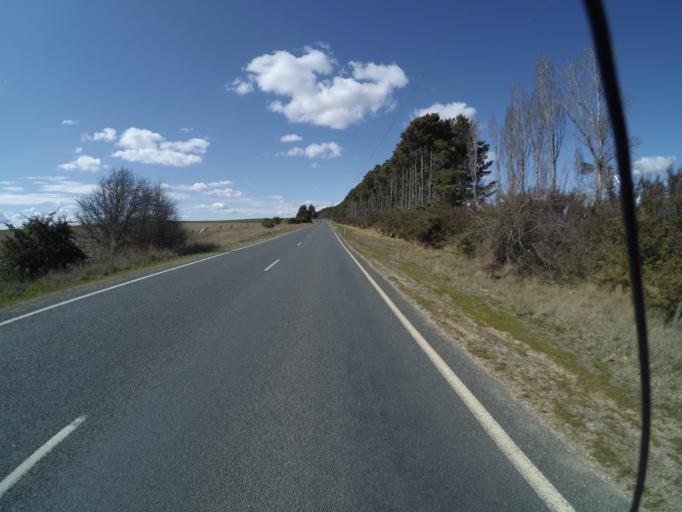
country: AU
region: New South Wales
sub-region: Palerang
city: Bungendore
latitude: -35.2237
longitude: 149.4570
